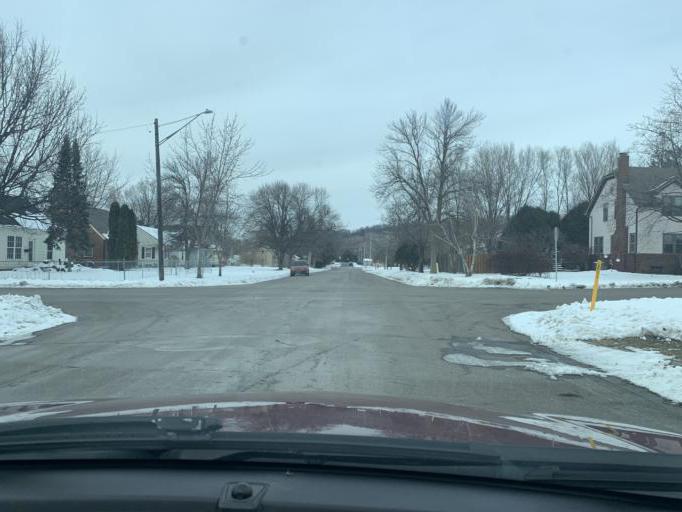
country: US
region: Minnesota
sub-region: Washington County
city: Saint Paul Park
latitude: 44.8459
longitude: -92.9900
